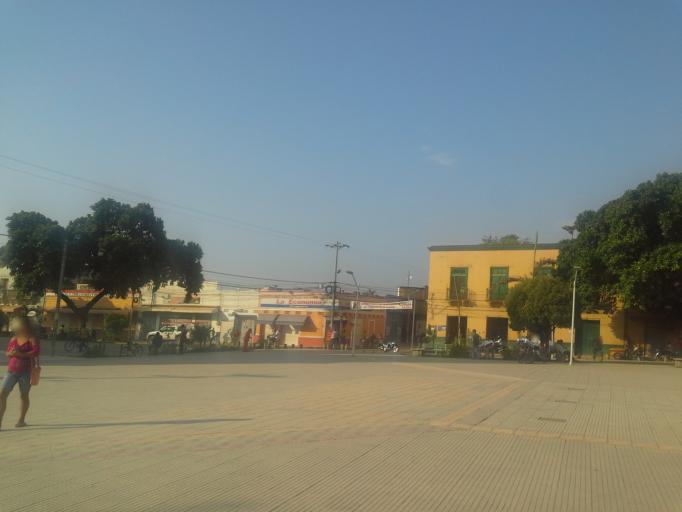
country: CO
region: Bolivar
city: El Carmen de Bolivar
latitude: 9.7163
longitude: -75.1211
